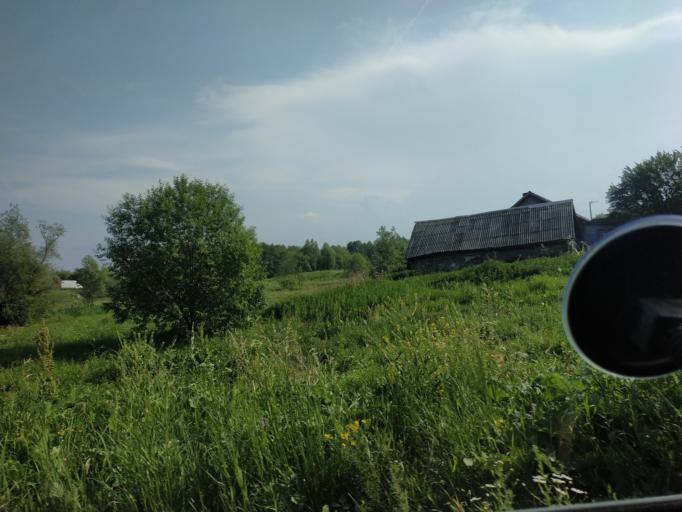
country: RU
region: Moskovskaya
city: Yakovlevskoye
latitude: 55.4259
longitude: 37.9517
